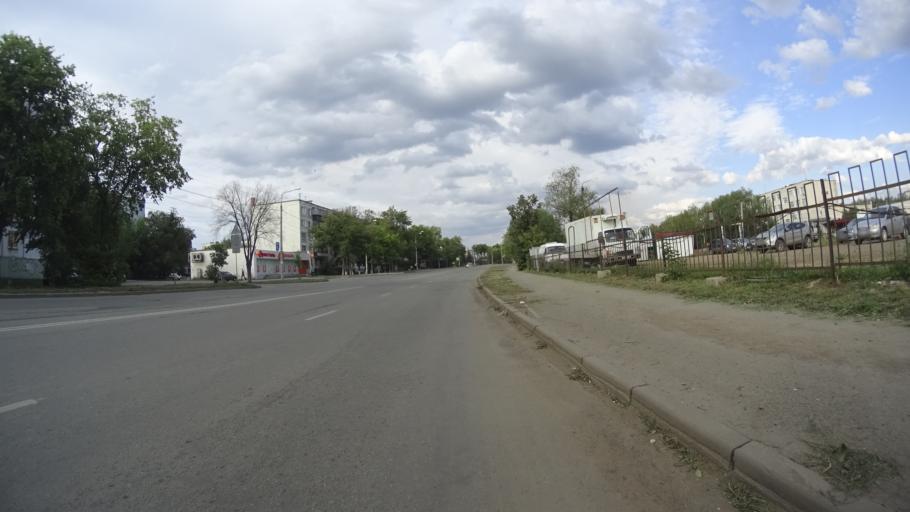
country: RU
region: Chelyabinsk
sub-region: Gorod Chelyabinsk
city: Chelyabinsk
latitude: 55.2010
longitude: 61.3200
